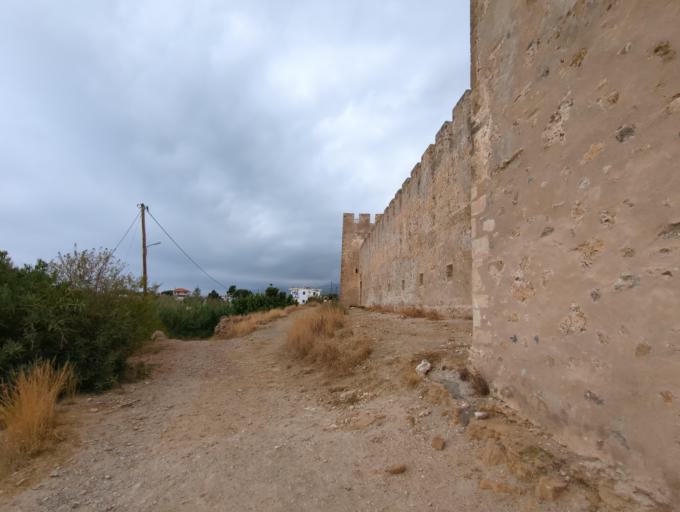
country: GR
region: Crete
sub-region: Nomos Chanias
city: Chora Sfakion
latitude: 35.1818
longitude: 24.2343
